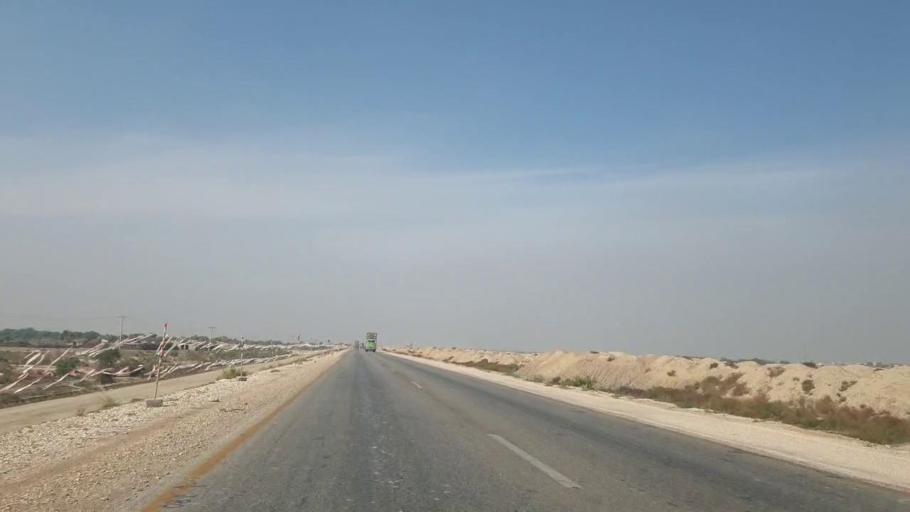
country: PK
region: Sindh
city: Sann
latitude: 25.9439
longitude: 68.2020
